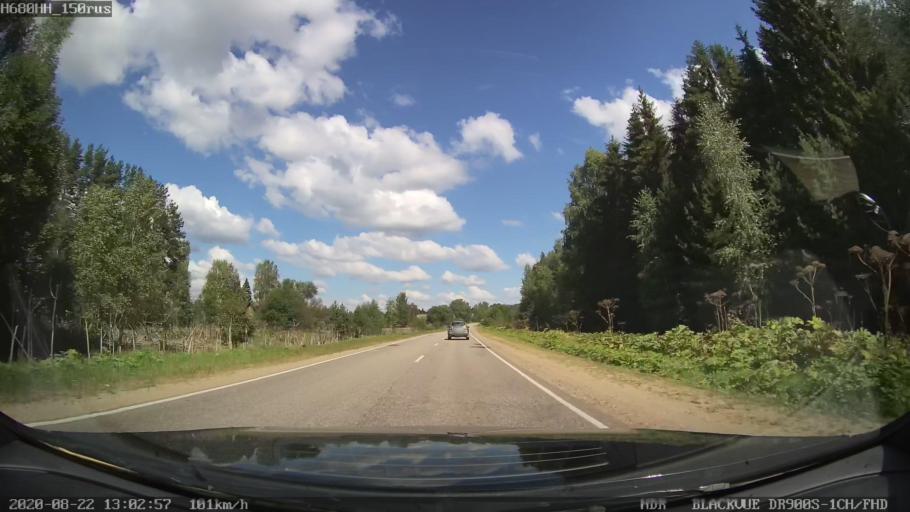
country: RU
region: Tverskaya
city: Bezhetsk
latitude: 57.6558
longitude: 36.4045
